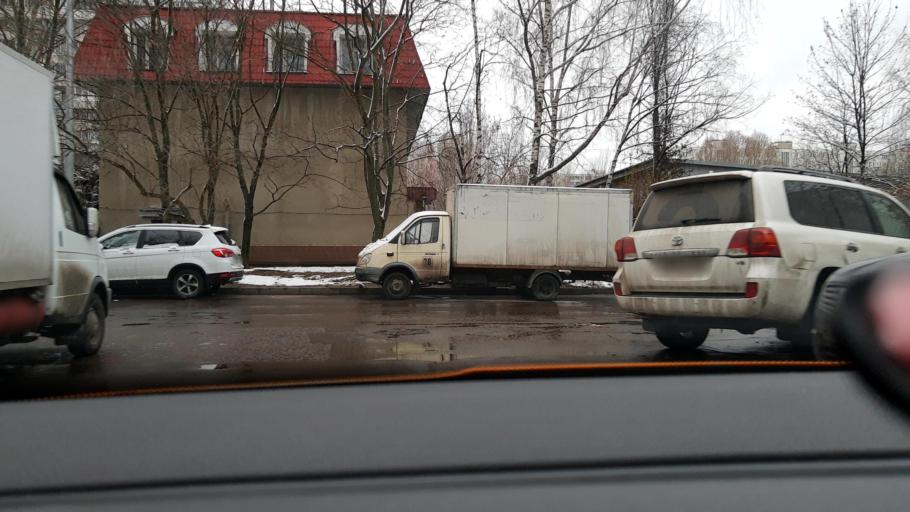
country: RU
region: Moscow
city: Strogino
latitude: 55.8063
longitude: 37.3996
